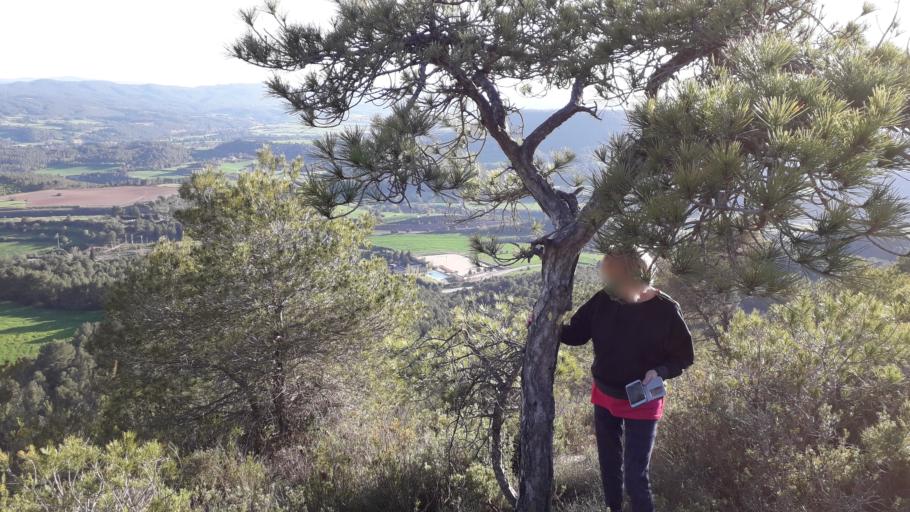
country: ES
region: Catalonia
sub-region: Provincia de Barcelona
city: Jorba
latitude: 41.6053
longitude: 1.5587
